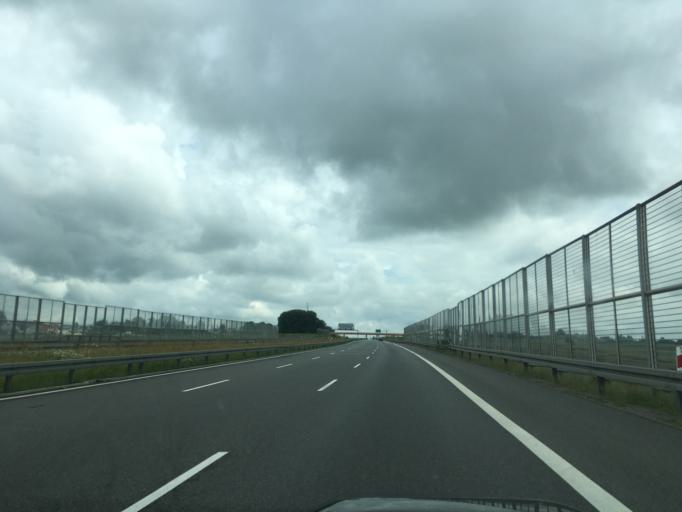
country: PL
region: Lublin Voivodeship
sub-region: Powiat lubelski
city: Lublin
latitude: 51.2977
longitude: 22.5313
